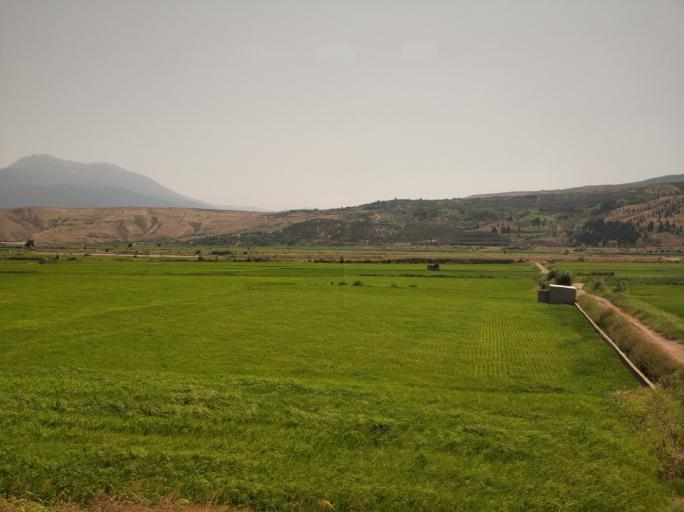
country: IR
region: Gilan
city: Pa'in-e Bazar-e Rudbar
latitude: 36.8762
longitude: 49.4948
